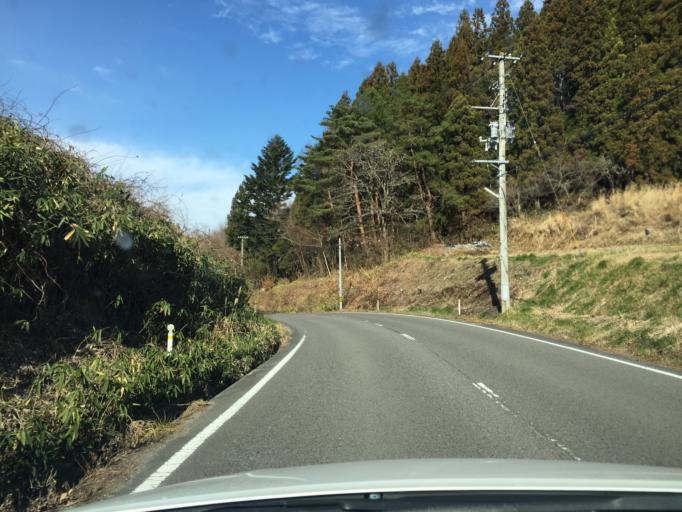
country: JP
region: Fukushima
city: Funehikimachi-funehiki
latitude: 37.2744
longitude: 140.5826
